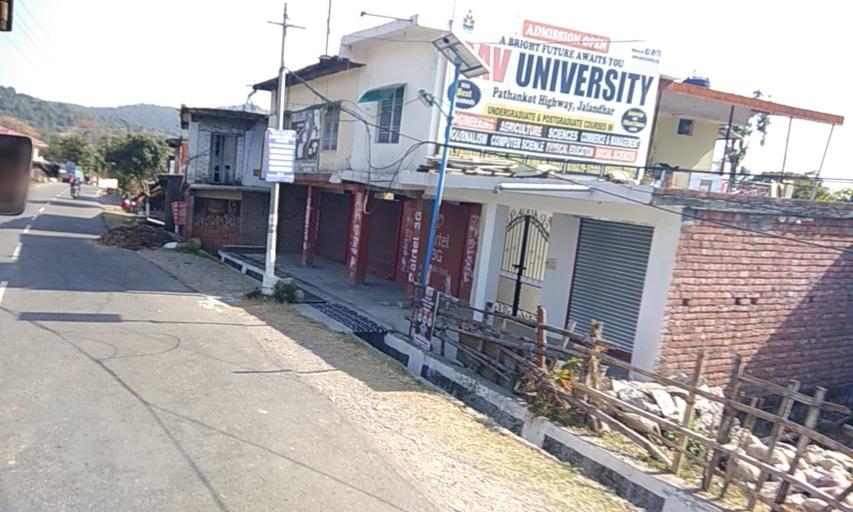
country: IN
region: Himachal Pradesh
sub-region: Kangra
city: Dharmsala
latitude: 32.1589
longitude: 76.4107
